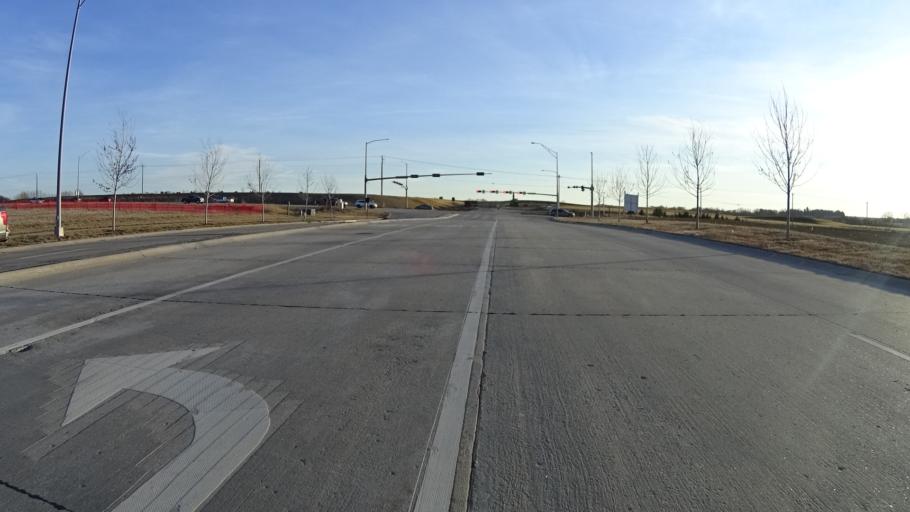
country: US
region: Nebraska
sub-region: Sarpy County
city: Chalco
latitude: 41.1486
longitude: -96.1100
